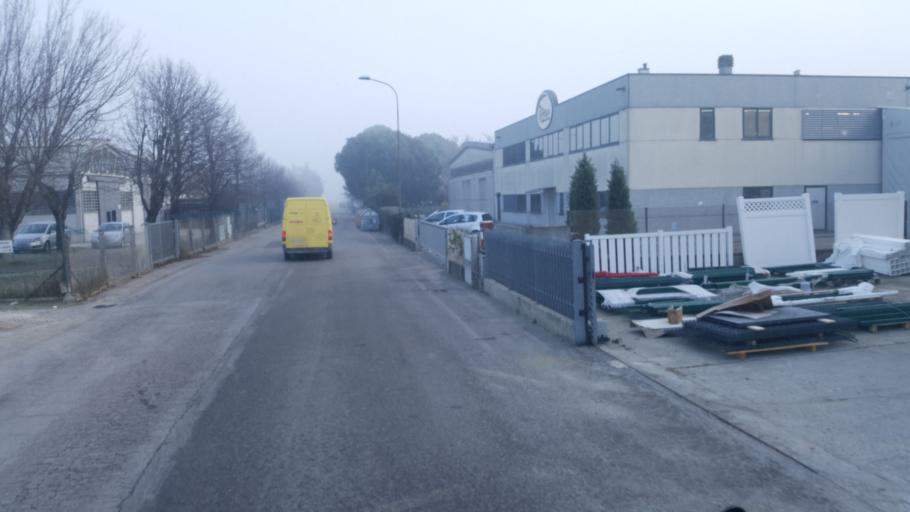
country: IT
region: Emilia-Romagna
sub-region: Provincia di Ravenna
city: Bagnacavallo
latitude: 44.4093
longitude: 11.9985
